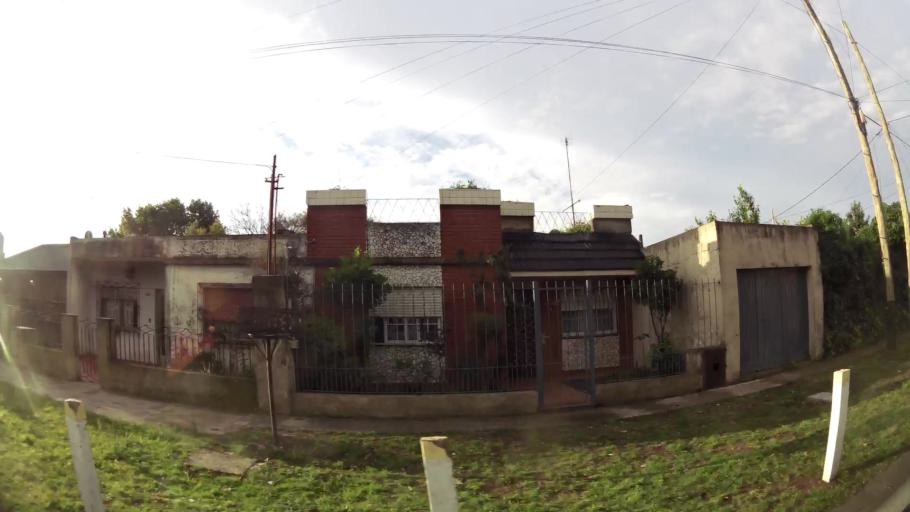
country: AR
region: Buenos Aires
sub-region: Partido de Lomas de Zamora
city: Lomas de Zamora
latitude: -34.7506
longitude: -58.3545
